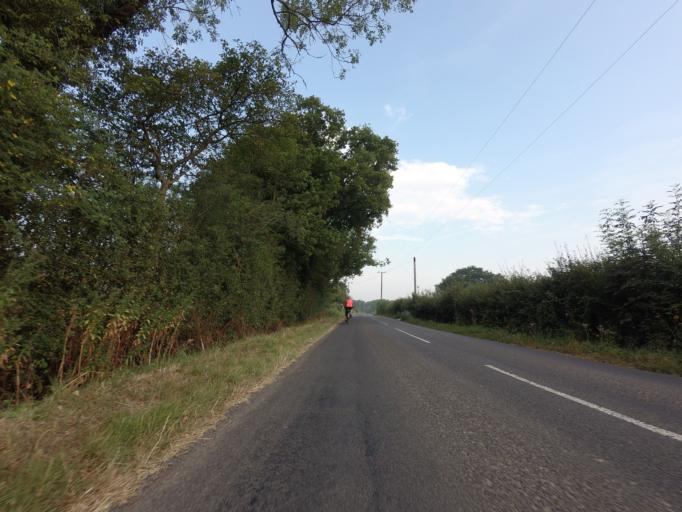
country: GB
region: England
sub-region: Kent
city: Tenterden
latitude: 51.1144
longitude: 0.7726
